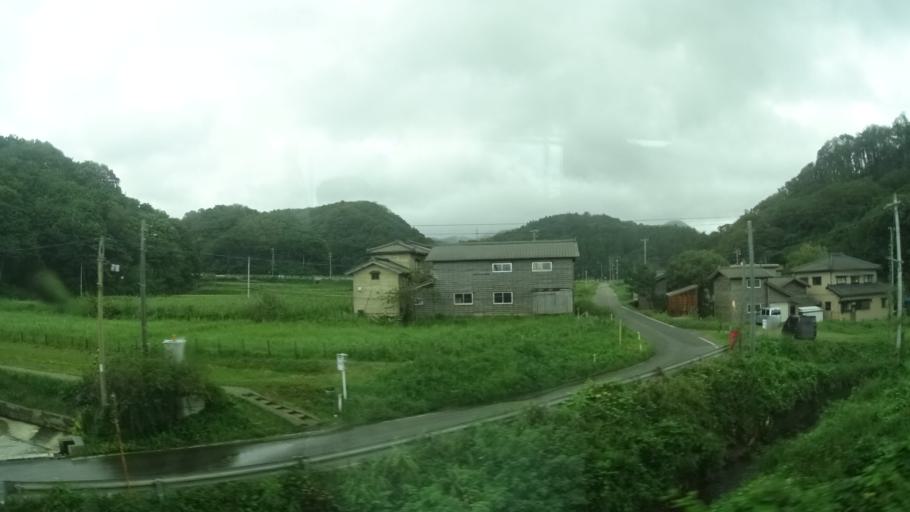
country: JP
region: Niigata
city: Murakami
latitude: 38.4950
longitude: 139.5188
